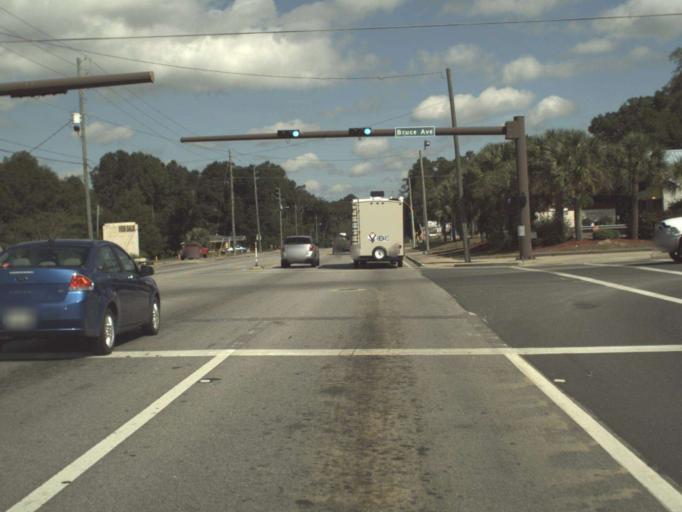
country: US
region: Florida
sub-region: Walton County
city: DeFuniak Springs
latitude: 30.7119
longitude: -86.1227
